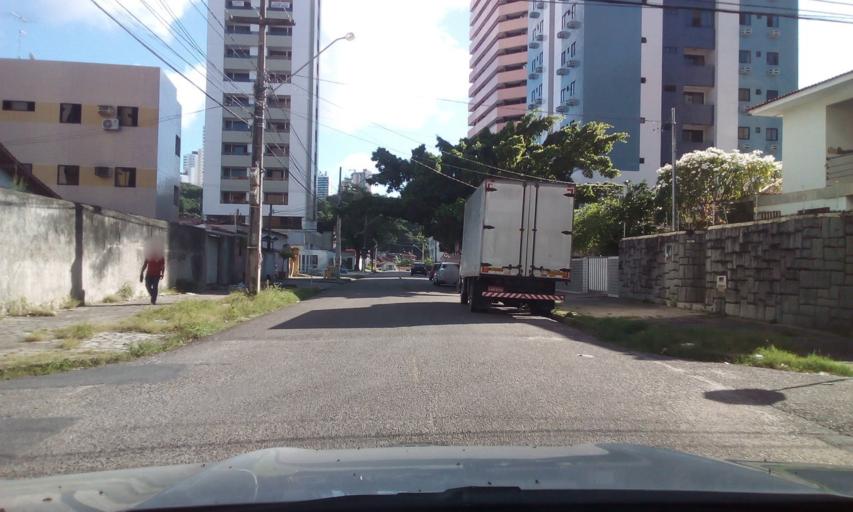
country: BR
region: Paraiba
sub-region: Joao Pessoa
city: Joao Pessoa
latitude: -7.1102
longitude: -34.8331
